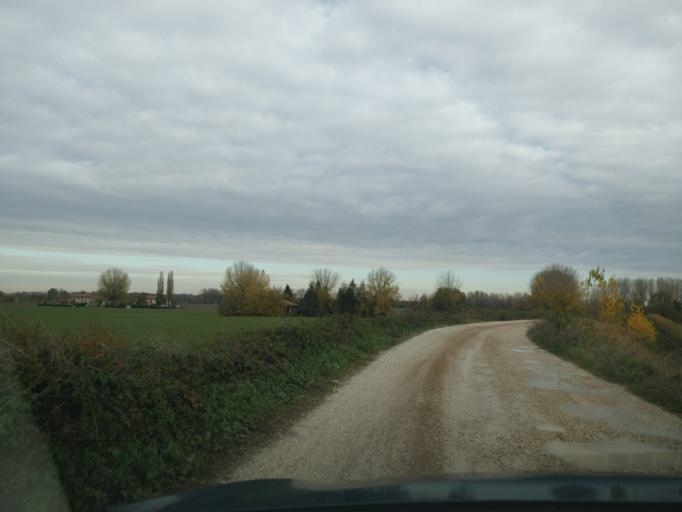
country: IT
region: Emilia-Romagna
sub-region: Provincia di Bologna
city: Padulle
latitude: 44.6336
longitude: 11.2998
